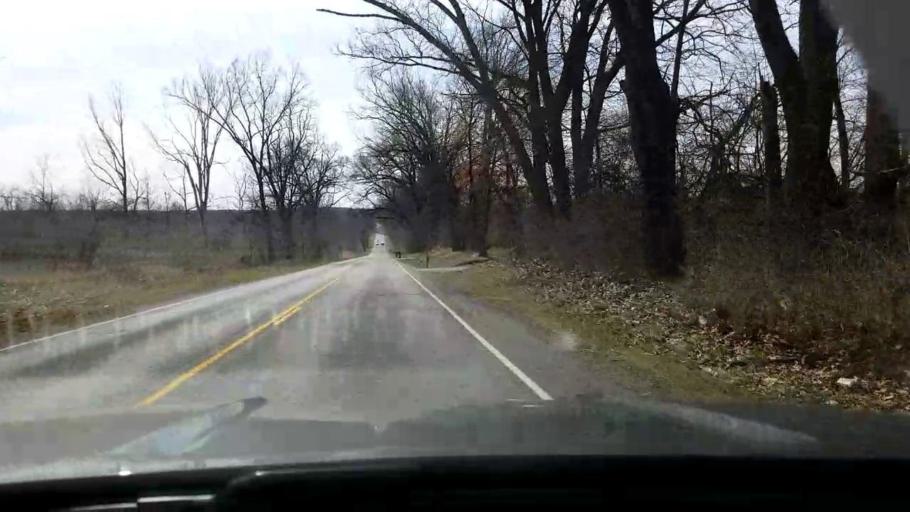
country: US
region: Michigan
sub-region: Jackson County
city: Spring Arbor
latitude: 42.2104
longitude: -84.5213
